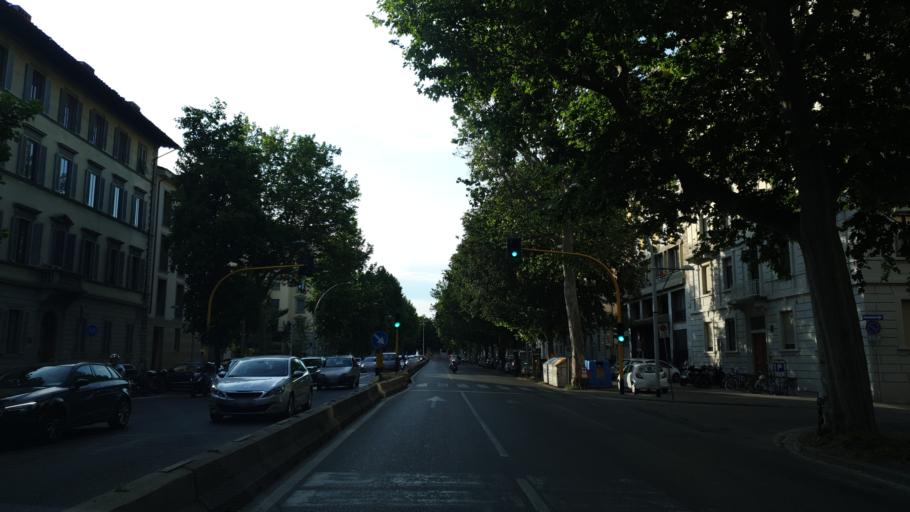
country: IT
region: Tuscany
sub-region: Province of Florence
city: Florence
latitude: 43.7811
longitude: 11.2646
